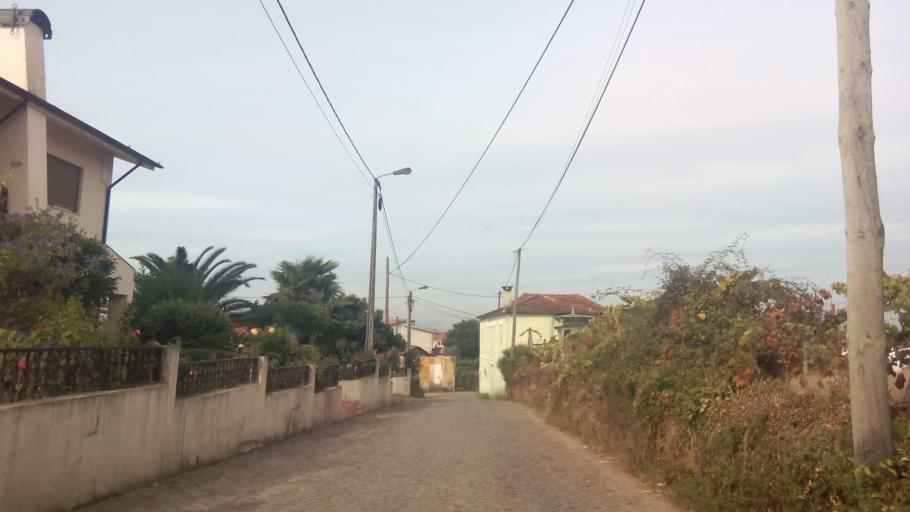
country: PT
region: Porto
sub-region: Paredes
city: Gandra
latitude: 41.1860
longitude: -8.4283
